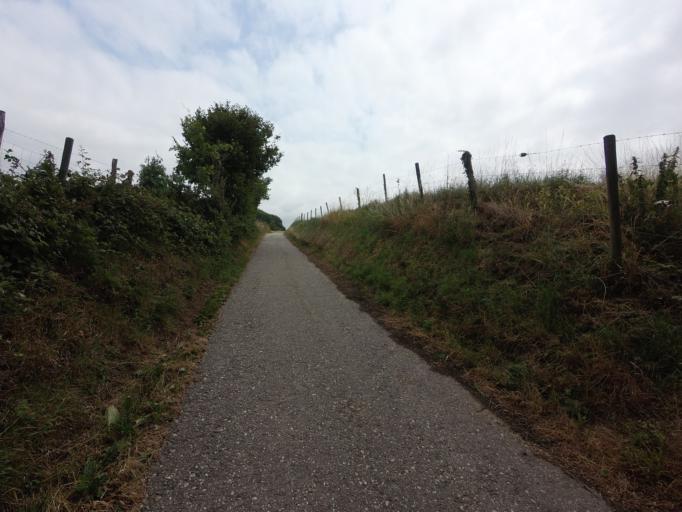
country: NL
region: Limburg
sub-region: Eijsden-Margraten
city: Margraten
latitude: 50.8162
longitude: 5.7993
